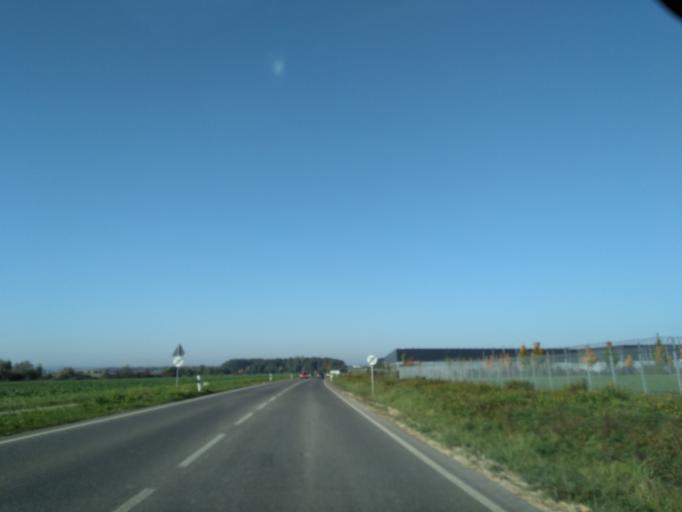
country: DE
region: Baden-Wuerttemberg
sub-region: Regierungsbezirk Stuttgart
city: Oberriexingen
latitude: 48.9502
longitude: 9.0456
